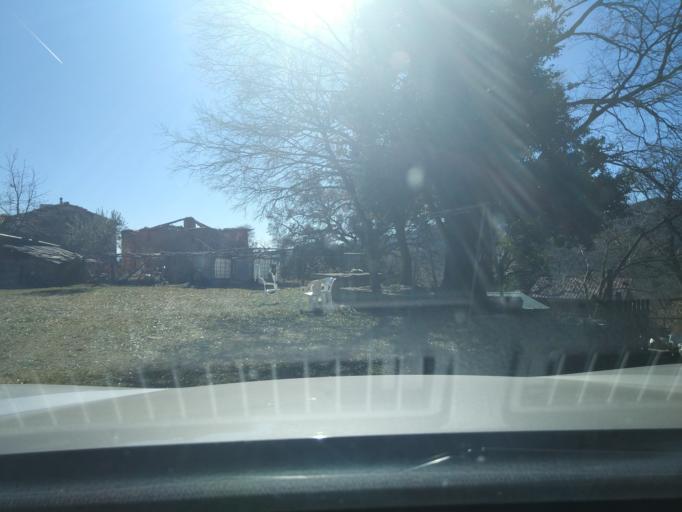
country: ES
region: Aragon
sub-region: Provincia de Huesca
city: Palo
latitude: 42.3113
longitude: 0.3406
